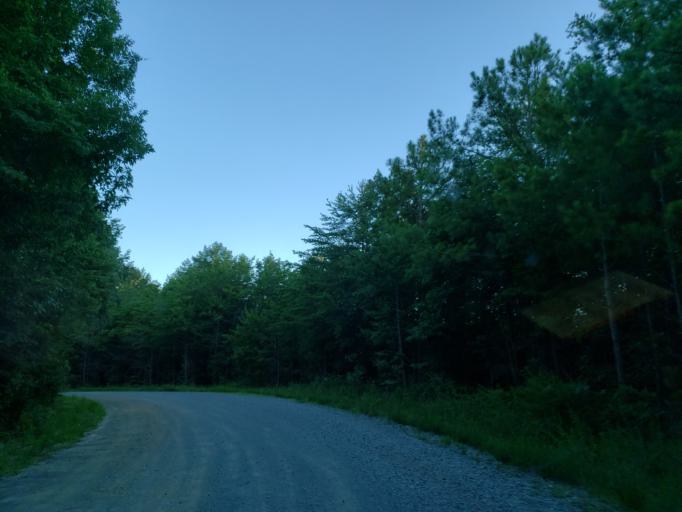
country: US
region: Georgia
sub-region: Bartow County
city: Euharlee
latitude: 34.0685
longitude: -84.8588
